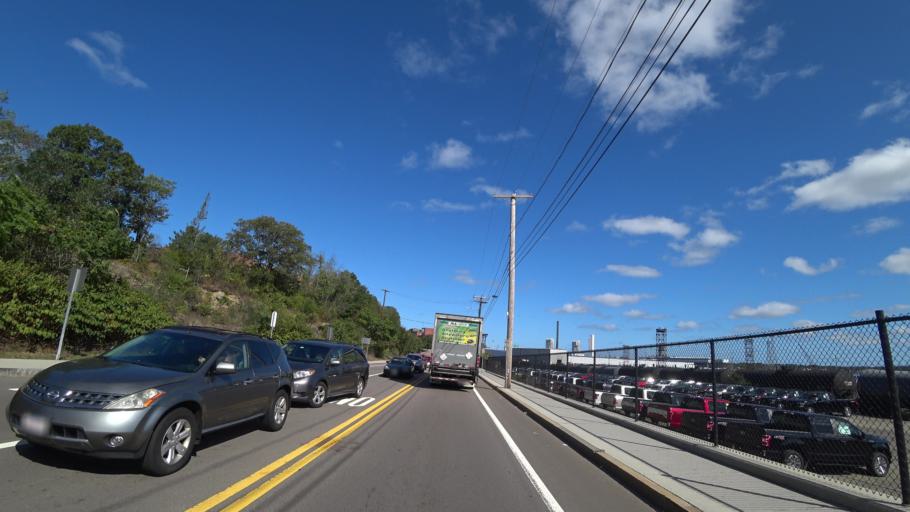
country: US
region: Massachusetts
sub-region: Norfolk County
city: Braintree
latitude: 42.2373
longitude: -70.9803
